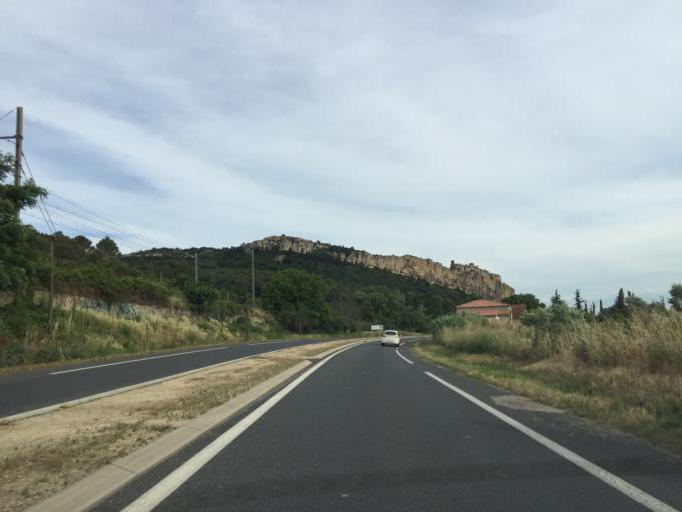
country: FR
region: Provence-Alpes-Cote d'Azur
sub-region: Departement du Vaucluse
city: Mornas
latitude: 44.2154
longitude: 4.7246
